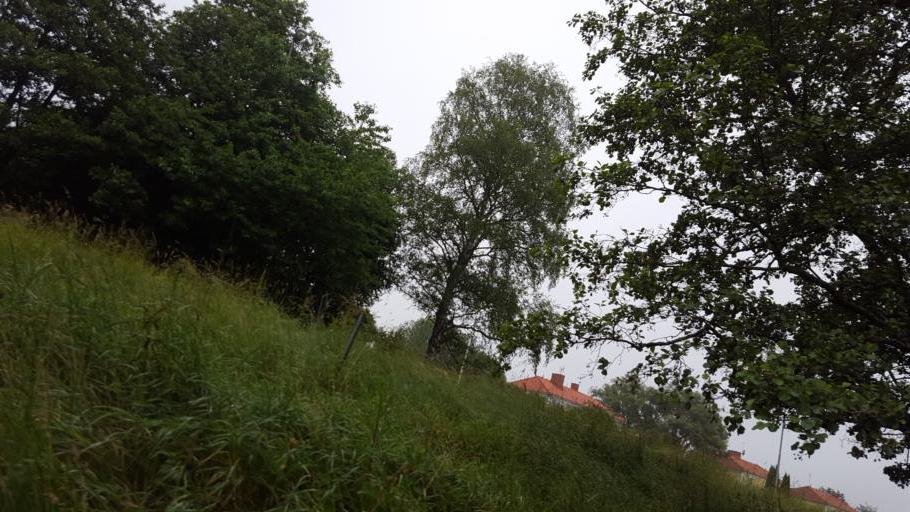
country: SE
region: Stockholm
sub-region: Upplands Vasby Kommun
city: Upplands Vaesby
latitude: 59.5083
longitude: 17.8826
